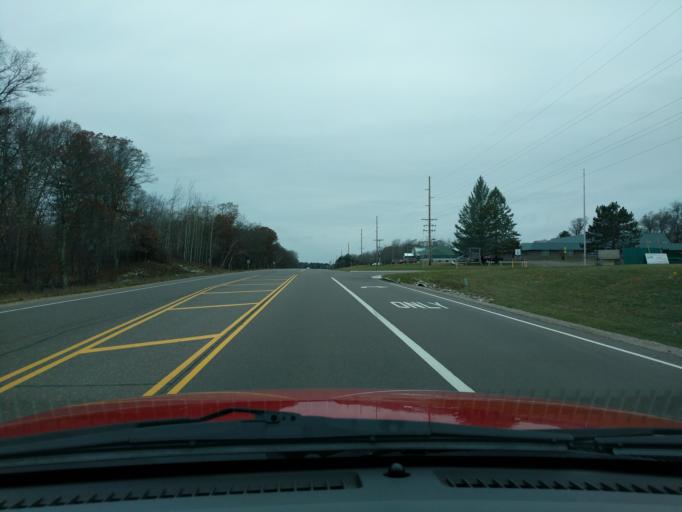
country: US
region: Wisconsin
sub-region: Burnett County
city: Siren
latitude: 45.8088
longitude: -92.2036
